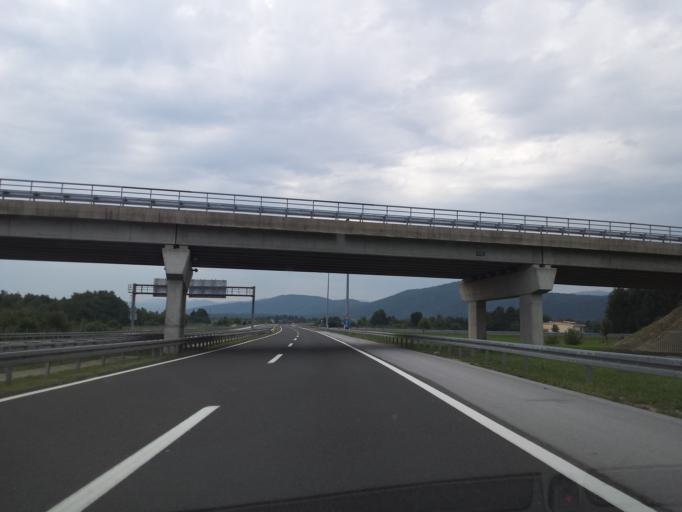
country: HR
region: Karlovacka
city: Ostarije
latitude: 45.2392
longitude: 15.2683
